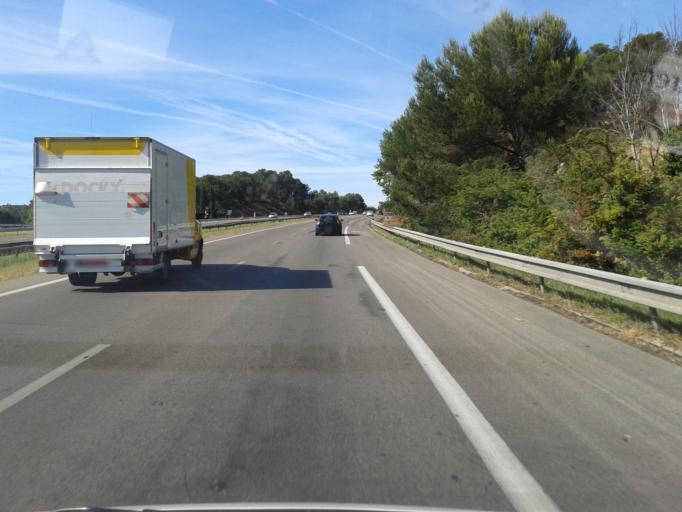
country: FR
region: Provence-Alpes-Cote d'Azur
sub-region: Departement des Bouches-du-Rhone
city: Cabries
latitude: 43.4346
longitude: 5.3952
